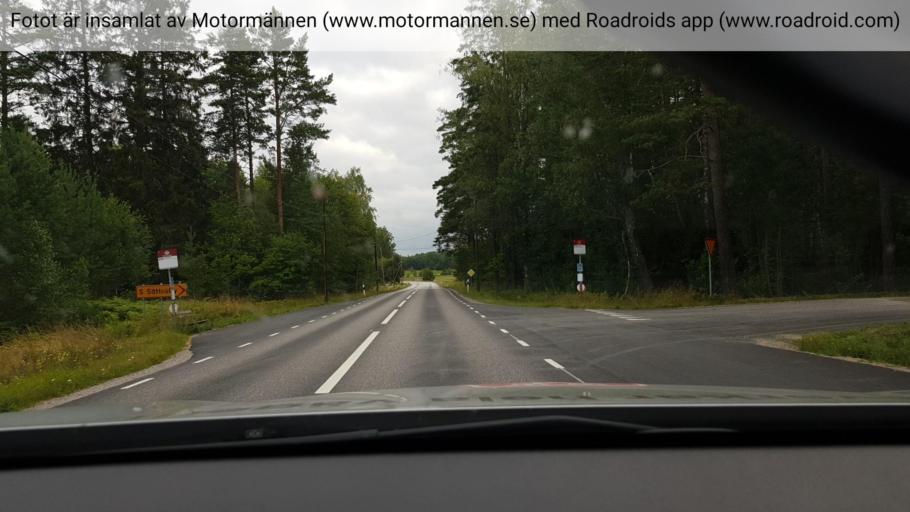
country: SE
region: Stockholm
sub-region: Norrtalje Kommun
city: Rimbo
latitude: 59.8276
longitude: 18.4413
